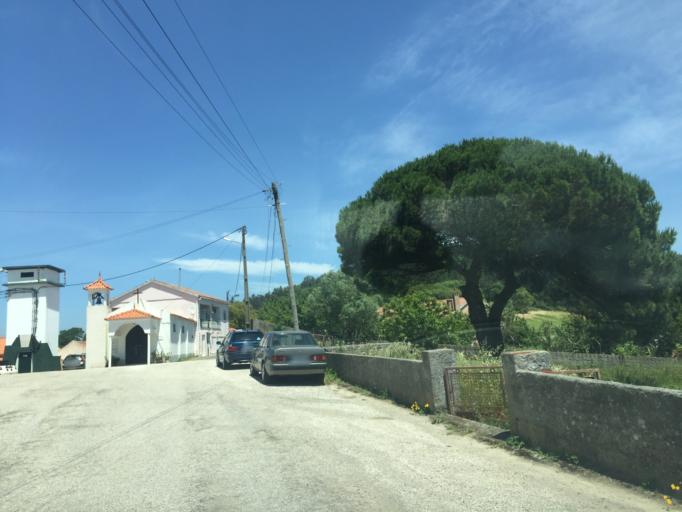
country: PT
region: Lisbon
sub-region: Mafra
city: Venda do Pinheiro
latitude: 38.8955
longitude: -9.2327
